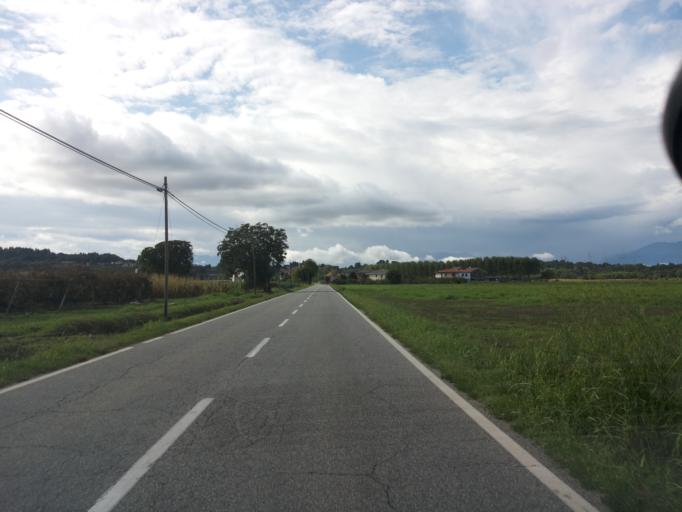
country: IT
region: Piedmont
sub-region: Provincia di Vercelli
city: Cigliano
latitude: 45.3219
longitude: 8.0141
